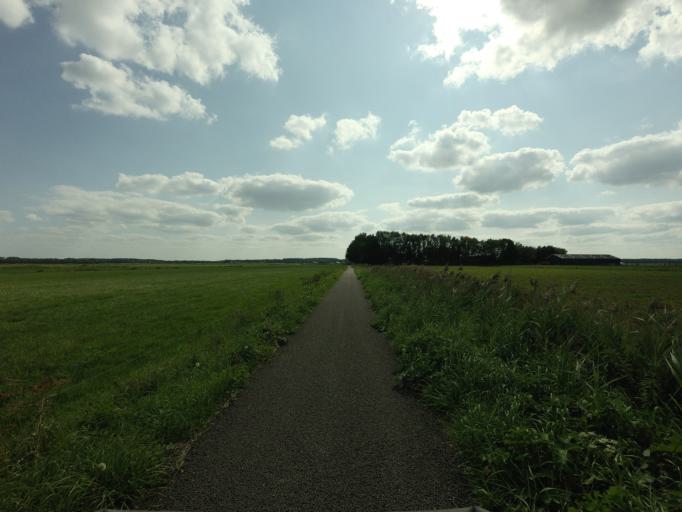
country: NL
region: Drenthe
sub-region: Gemeente Westerveld
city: Dwingeloo
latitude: 52.8523
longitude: 6.4663
